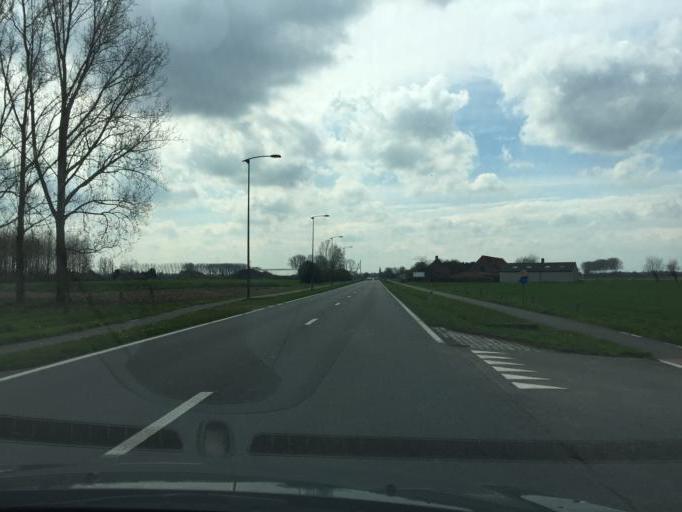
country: BE
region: Flanders
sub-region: Provincie West-Vlaanderen
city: Ruiselede
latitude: 51.0604
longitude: 3.4250
